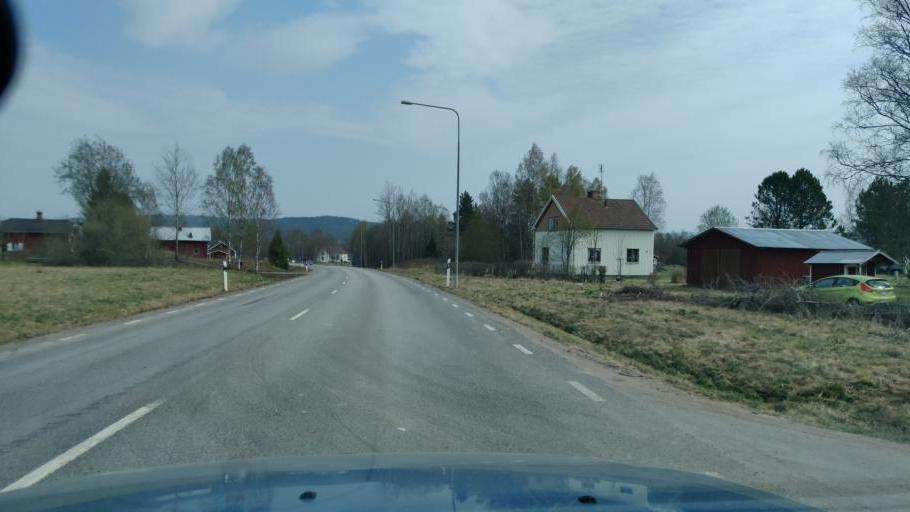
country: SE
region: Vaermland
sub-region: Munkfors Kommun
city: Munkfors
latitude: 59.8325
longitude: 13.5115
